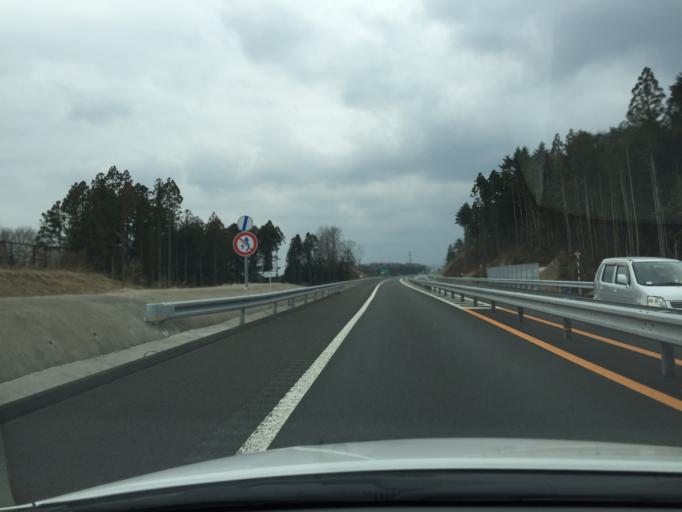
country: JP
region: Miyagi
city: Marumori
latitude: 37.8668
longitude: 140.8829
